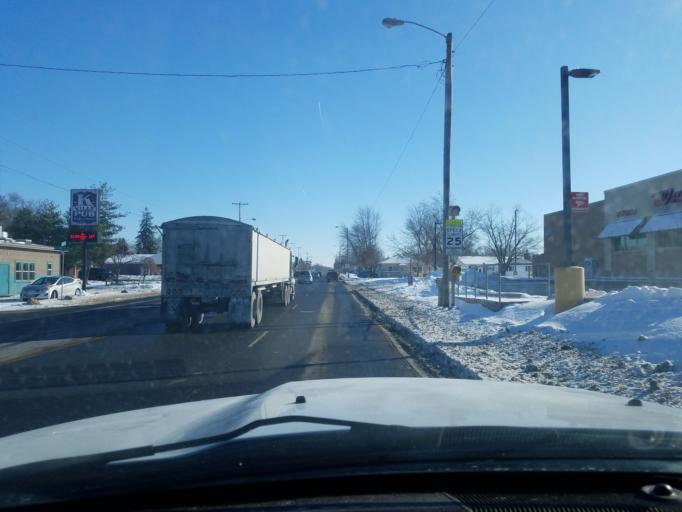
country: US
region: Indiana
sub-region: Noble County
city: Kendallville
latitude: 41.4523
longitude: -85.2672
